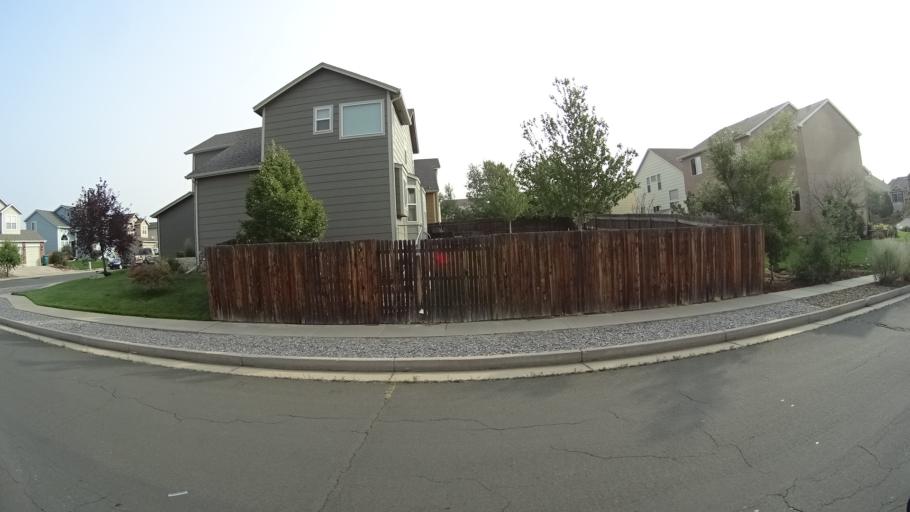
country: US
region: Colorado
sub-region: El Paso County
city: Cimarron Hills
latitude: 38.9346
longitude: -104.7273
